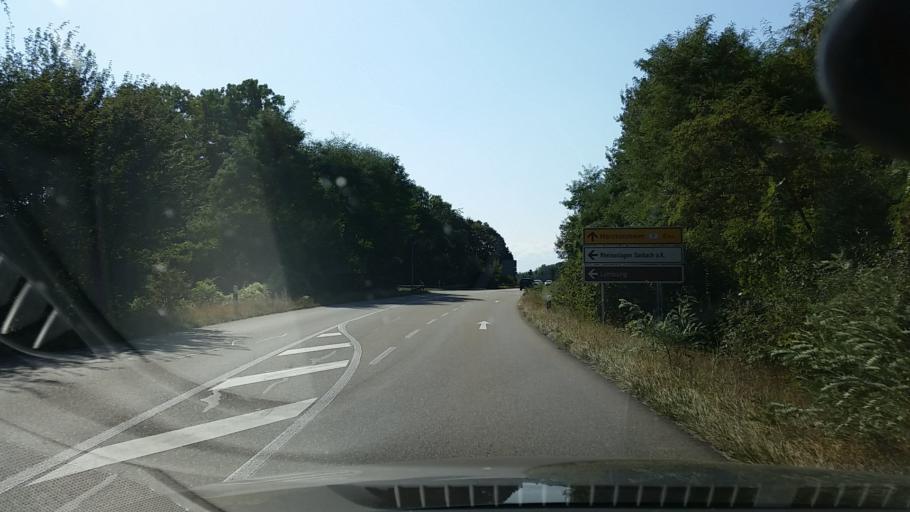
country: DE
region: Baden-Wuerttemberg
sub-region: Freiburg Region
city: Sasbach
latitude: 48.1544
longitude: 7.6034
